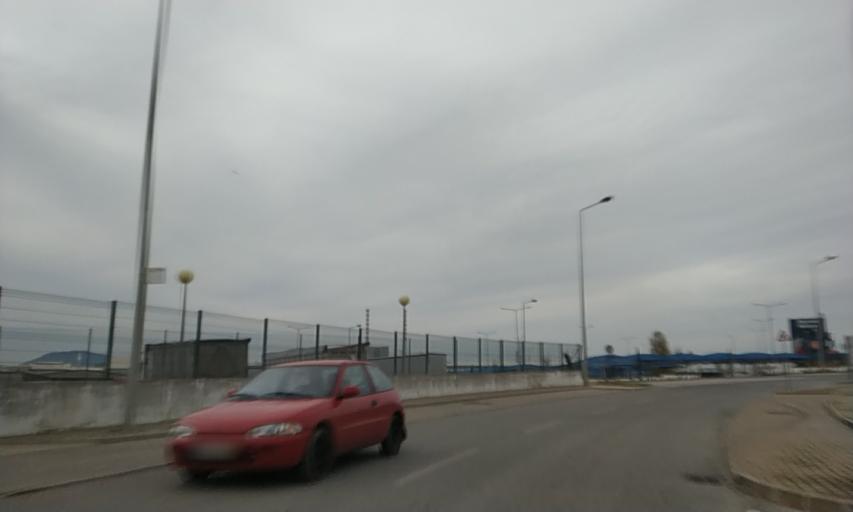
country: PT
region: Setubal
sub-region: Setubal
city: Setubal
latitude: 38.4973
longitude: -8.8292
